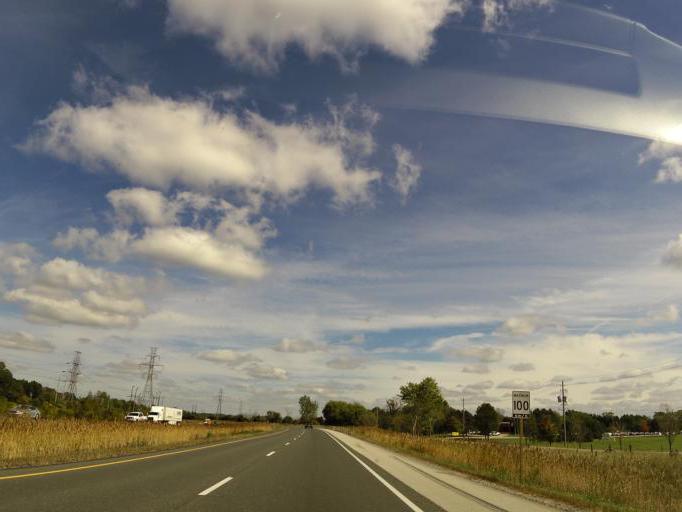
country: CA
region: Ontario
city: London
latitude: 42.8940
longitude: -81.2835
